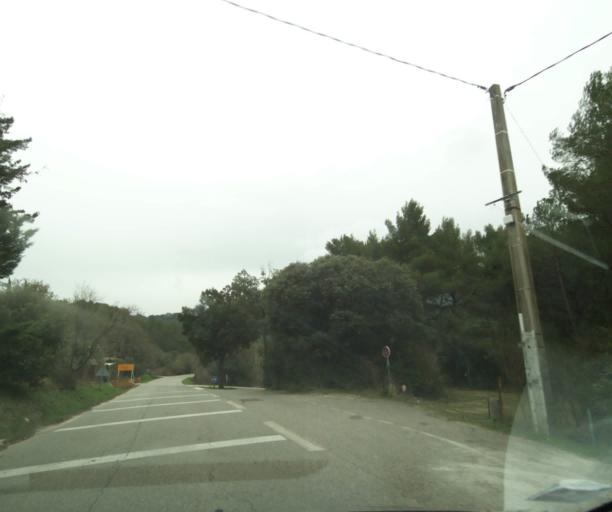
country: FR
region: Provence-Alpes-Cote d'Azur
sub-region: Departement des Bouches-du-Rhone
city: Chateauneuf-le-Rouge
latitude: 43.5542
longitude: 5.5783
